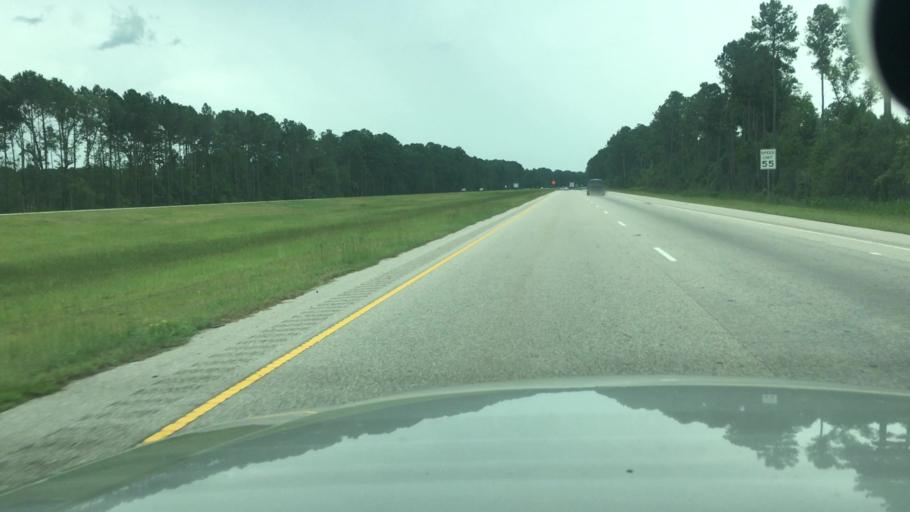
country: US
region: North Carolina
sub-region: Cumberland County
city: Vander
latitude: 34.9696
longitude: -78.8518
